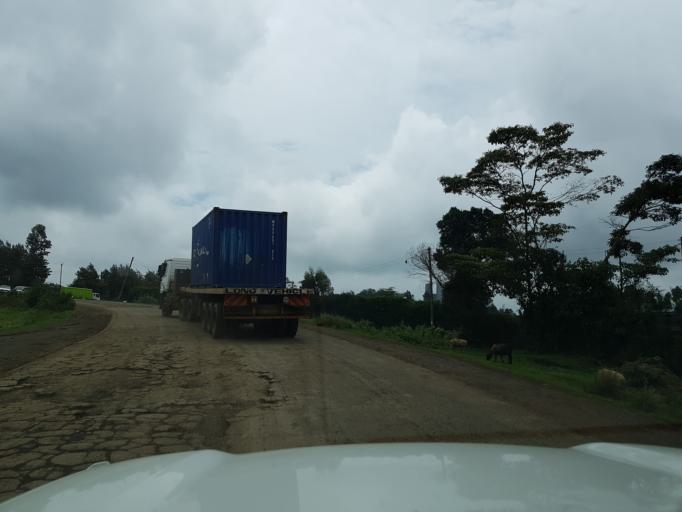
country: KE
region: Kiambu
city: Limuru
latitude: -1.1309
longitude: 36.6357
